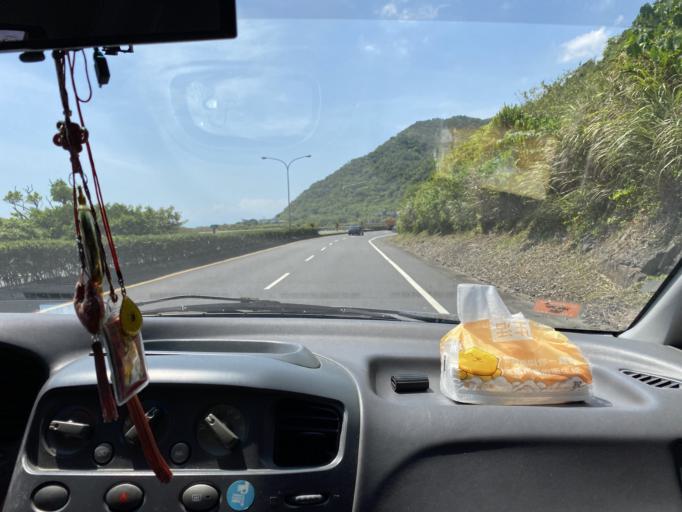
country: TW
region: Taiwan
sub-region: Yilan
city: Yilan
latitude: 24.9260
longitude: 121.8857
